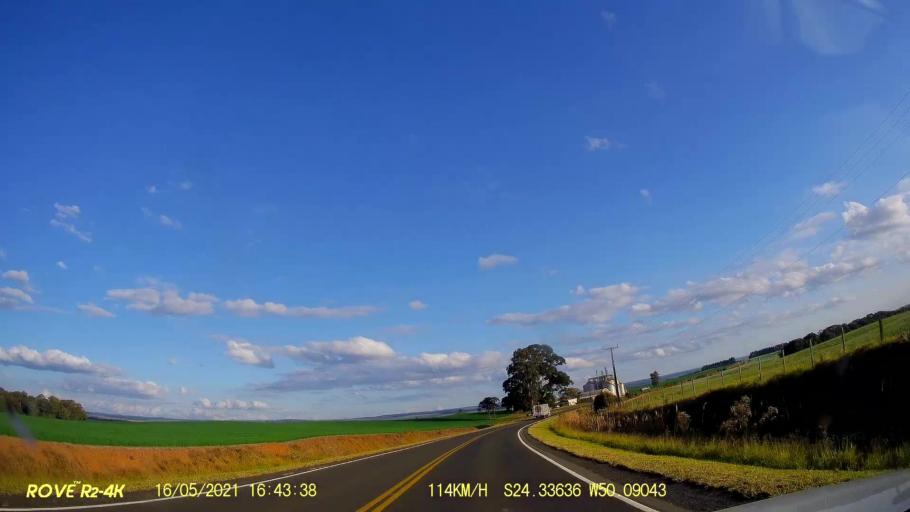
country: BR
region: Parana
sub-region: Pirai Do Sul
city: Pirai do Sul
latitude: -24.3364
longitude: -50.0904
